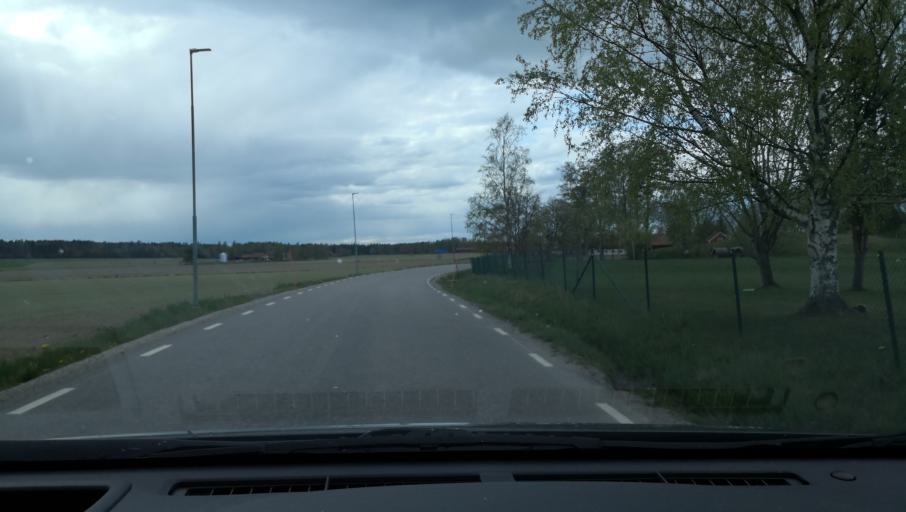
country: SE
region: Dalarna
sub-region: Avesta Kommun
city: Avesta
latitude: 60.0191
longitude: 16.2917
